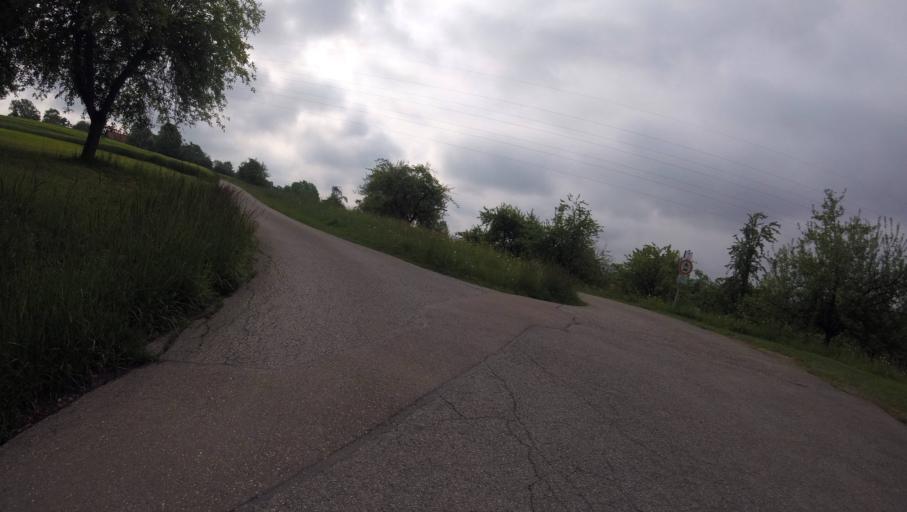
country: DE
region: Baden-Wuerttemberg
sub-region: Regierungsbezirk Stuttgart
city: Backnang
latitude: 48.9405
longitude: 9.4673
